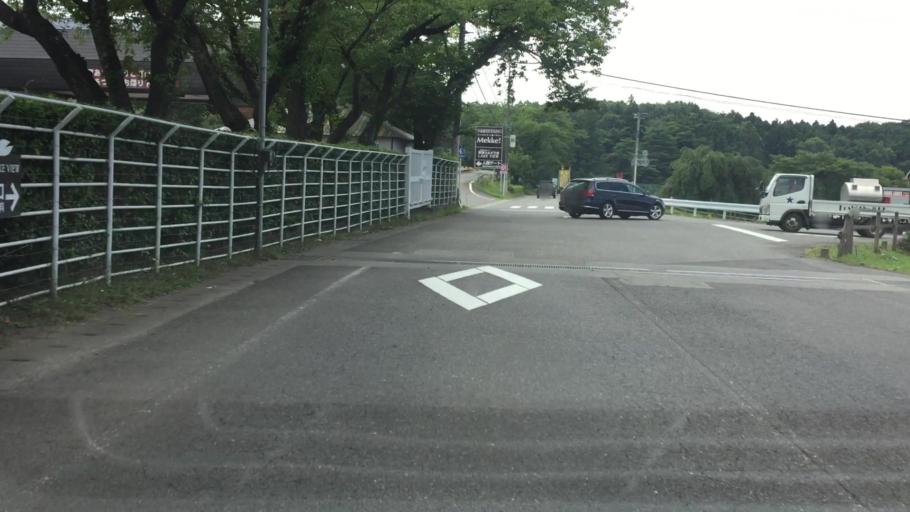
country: JP
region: Tochigi
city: Kuroiso
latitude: 37.0416
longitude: 140.0463
